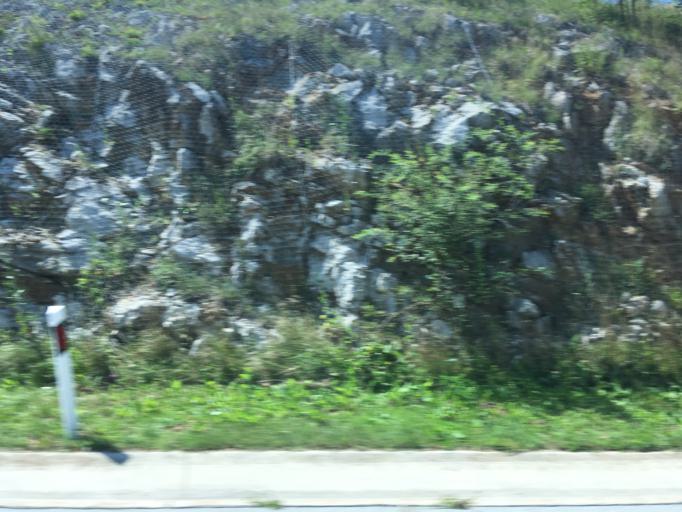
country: HR
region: Karlovacka
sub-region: Grad Ogulin
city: Ogulin
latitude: 45.3536
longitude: 15.2777
